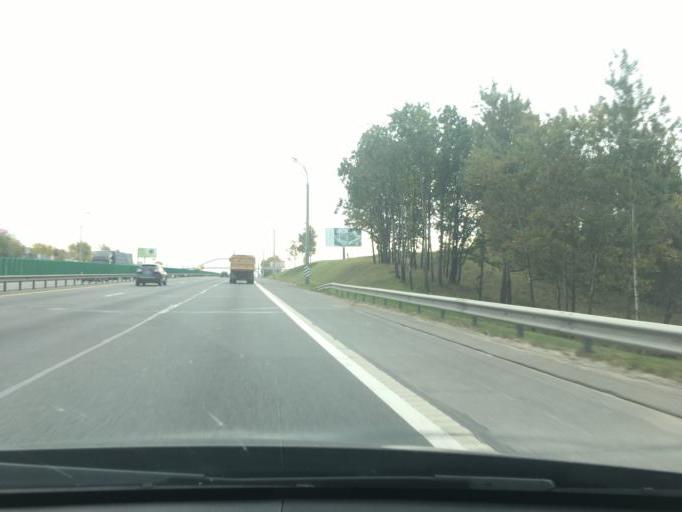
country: BY
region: Minsk
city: Malinovka
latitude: 53.8674
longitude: 27.4238
